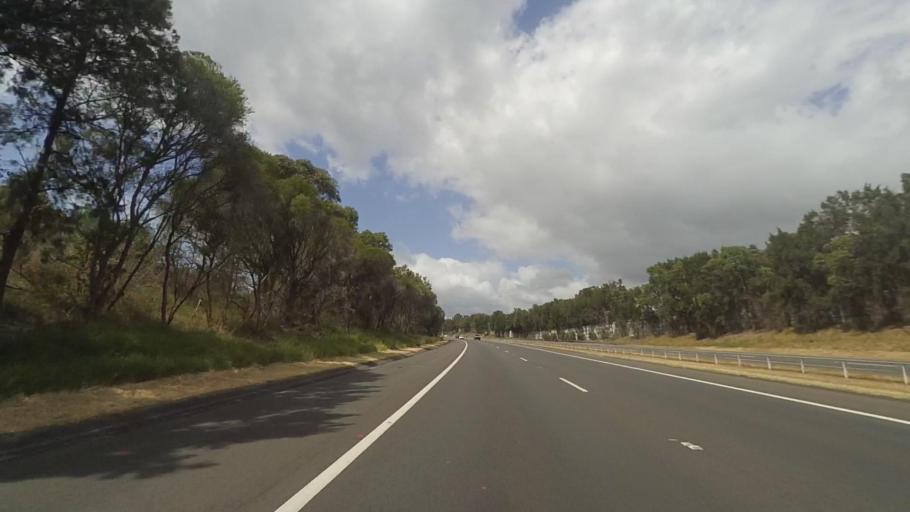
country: AU
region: New South Wales
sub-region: Wollongong
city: Dapto
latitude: -34.5057
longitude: 150.7906
